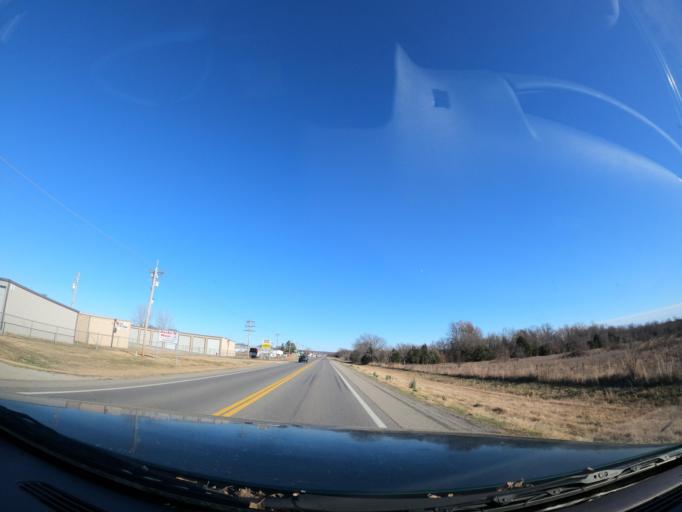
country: US
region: Oklahoma
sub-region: Pittsburg County
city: Longtown
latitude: 35.2392
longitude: -95.5219
